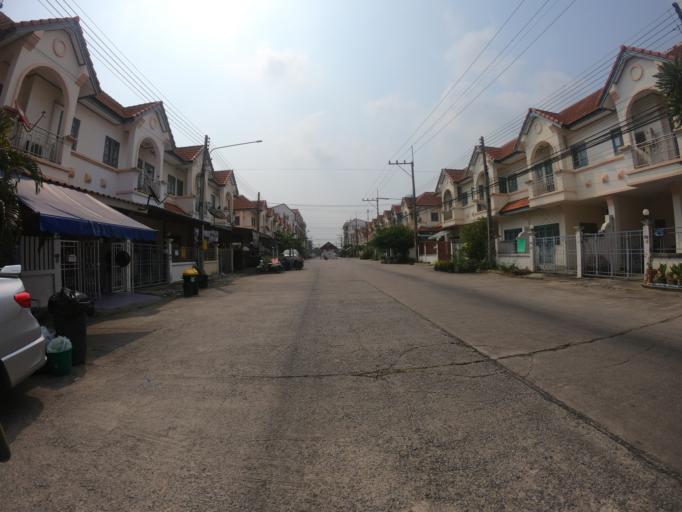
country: TH
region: Pathum Thani
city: Nong Suea
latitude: 14.0663
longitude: 100.8587
